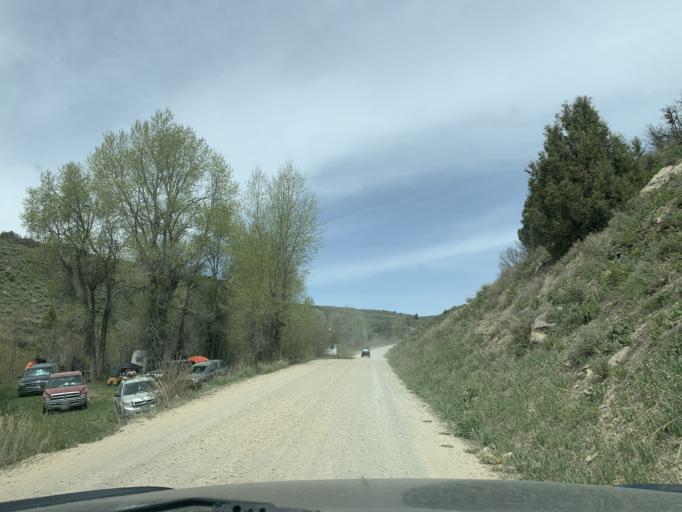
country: US
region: Utah
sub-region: Utah County
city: Mapleton
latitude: 40.1726
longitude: -111.3304
